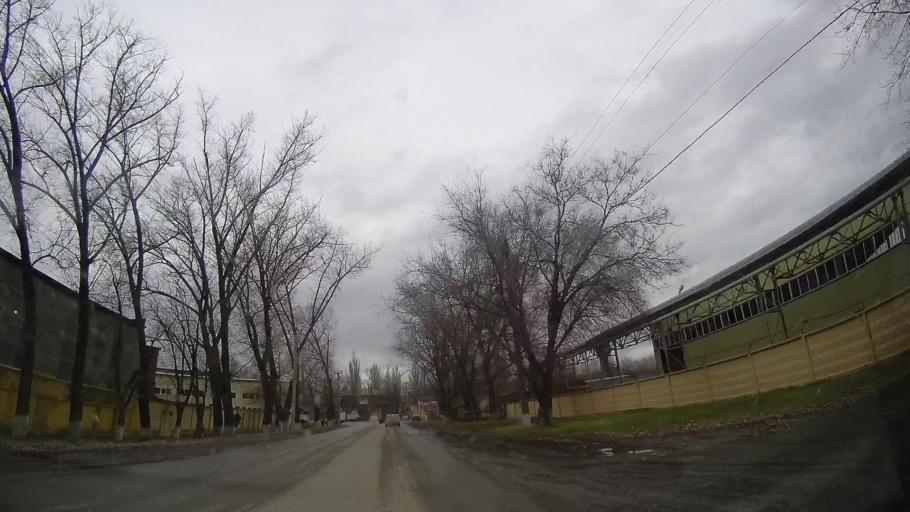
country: RU
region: Rostov
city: Bataysk
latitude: 47.1139
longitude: 39.7513
